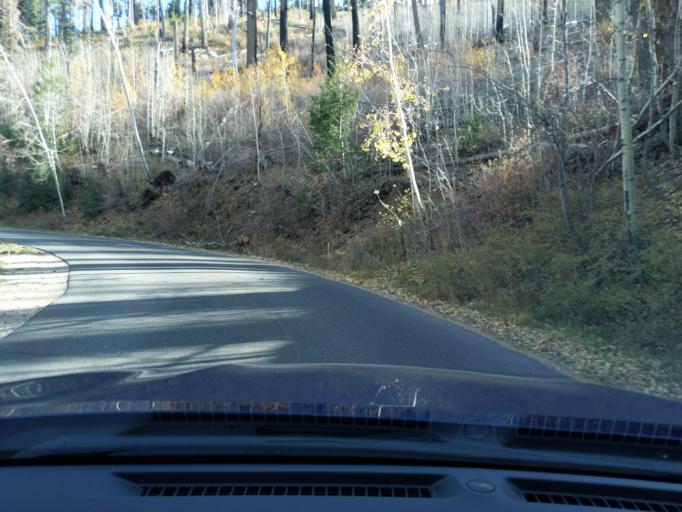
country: US
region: Arizona
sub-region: Pima County
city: Catalina
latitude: 32.4451
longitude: -110.7884
